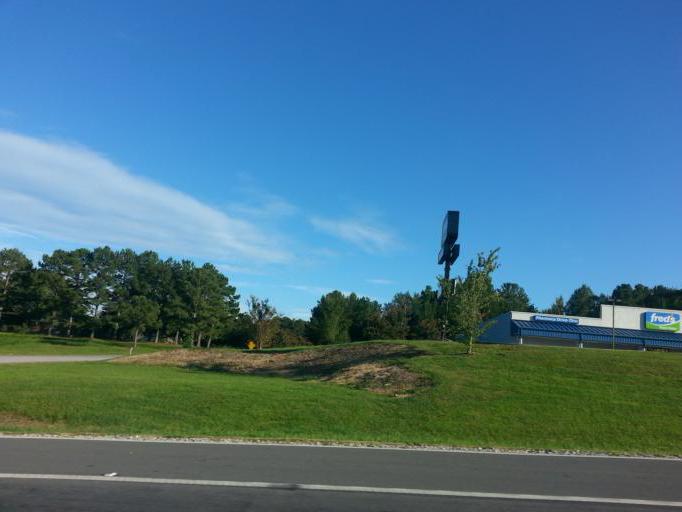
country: US
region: Alabama
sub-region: Lauderdale County
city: Killen
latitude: 34.8456
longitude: -87.5804
